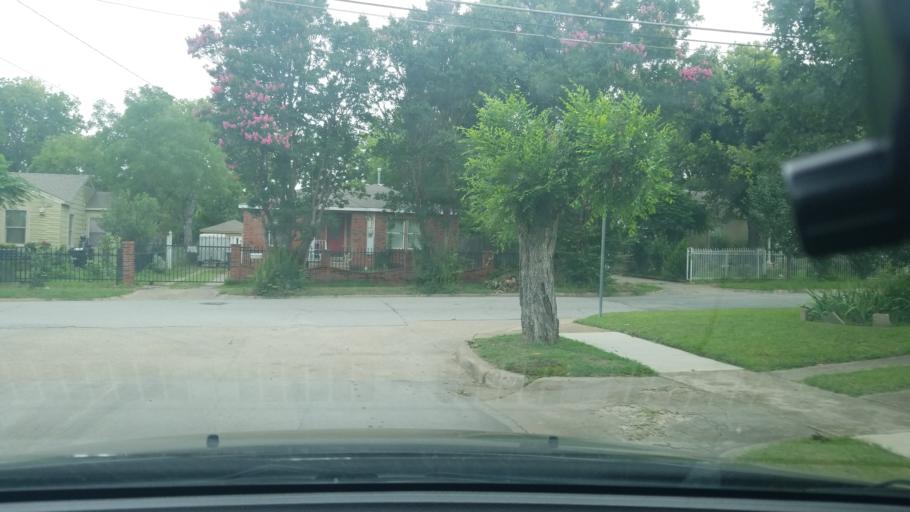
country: US
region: Texas
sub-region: Dallas County
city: Balch Springs
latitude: 32.7755
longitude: -96.6908
